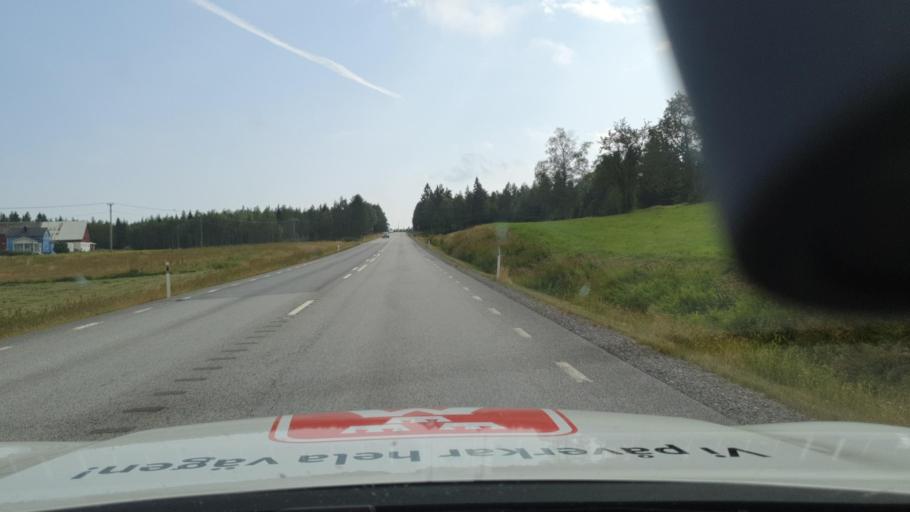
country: SE
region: Vaesterbotten
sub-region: Robertsfors Kommun
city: Robertsfors
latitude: 64.2105
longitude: 21.0173
